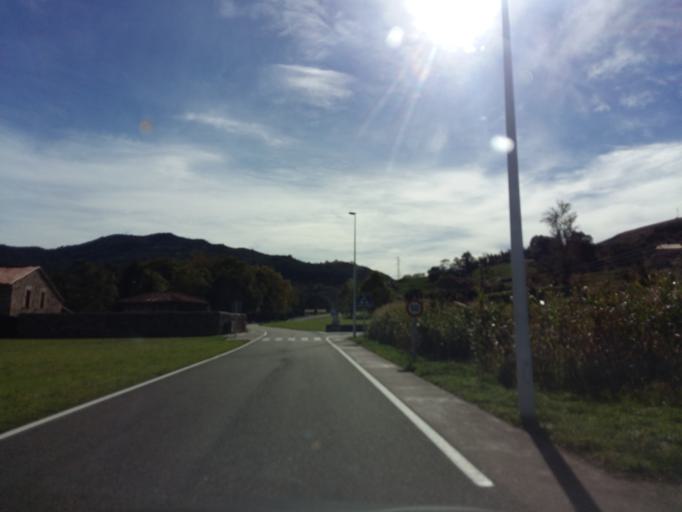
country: ES
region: Cantabria
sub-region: Provincia de Cantabria
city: San Vicente de la Barquera
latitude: 43.3050
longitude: -4.4673
